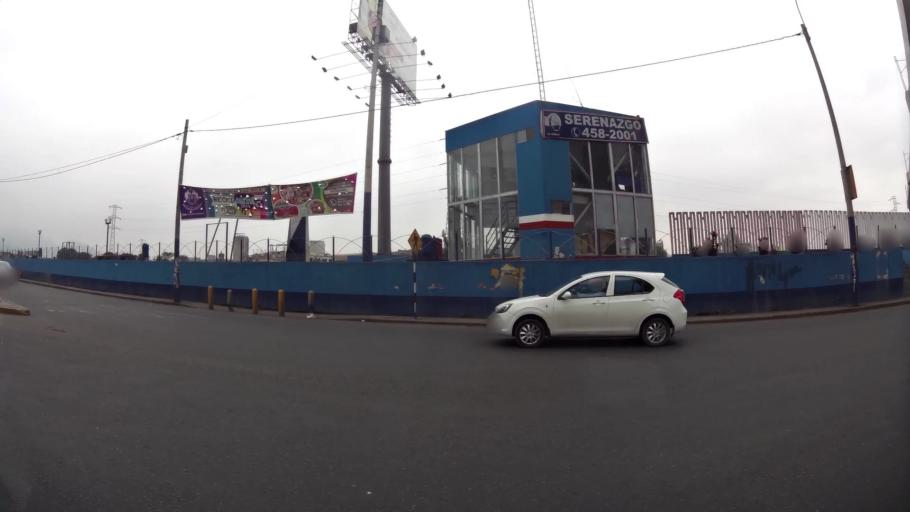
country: PE
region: Lima
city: Lima
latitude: -12.0322
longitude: -77.0120
